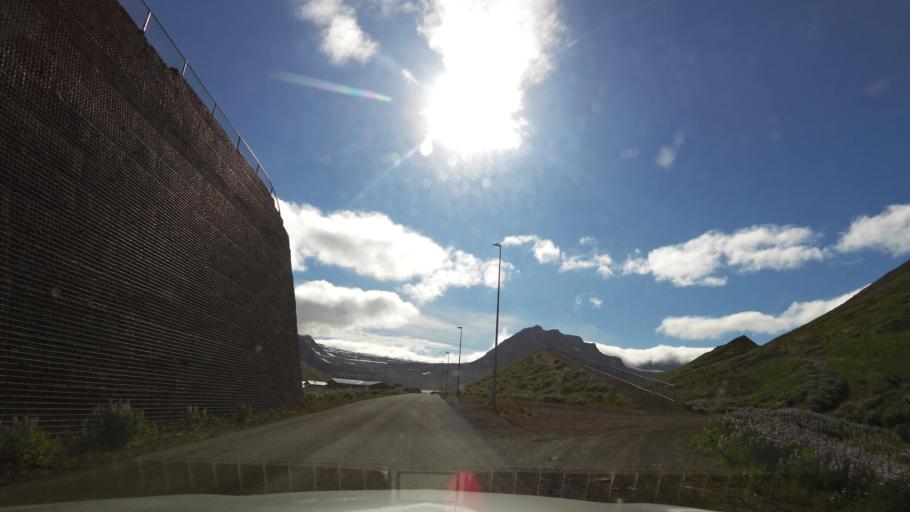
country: IS
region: Westfjords
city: Isafjoerdur
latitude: 66.1624
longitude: -23.2533
